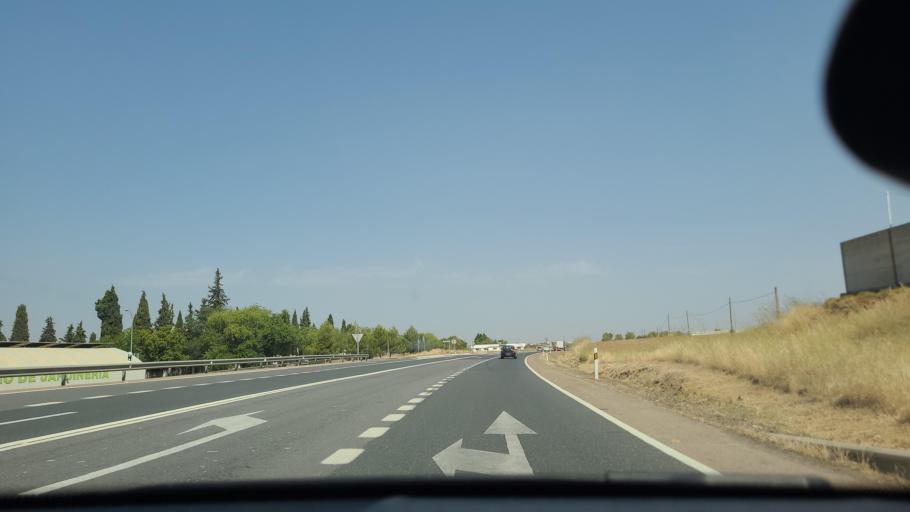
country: ES
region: Extremadura
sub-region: Provincia de Badajoz
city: Zafra
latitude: 38.4335
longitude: -6.4225
